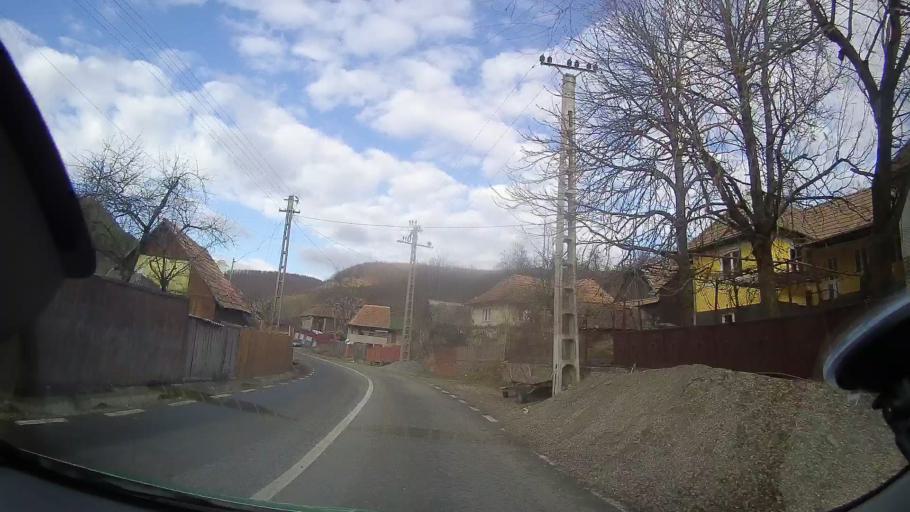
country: RO
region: Cluj
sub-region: Comuna Baisoara
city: Baisoara
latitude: 46.5818
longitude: 23.4560
